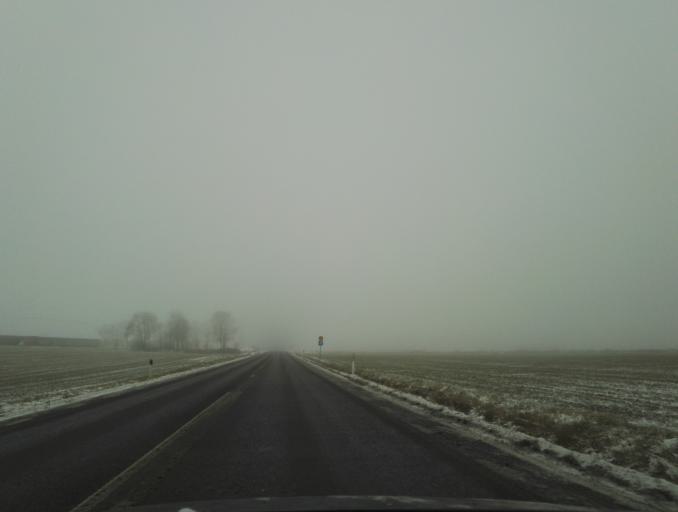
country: SE
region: Kronoberg
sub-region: Vaxjo Kommun
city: Gemla
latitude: 56.8502
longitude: 14.7221
